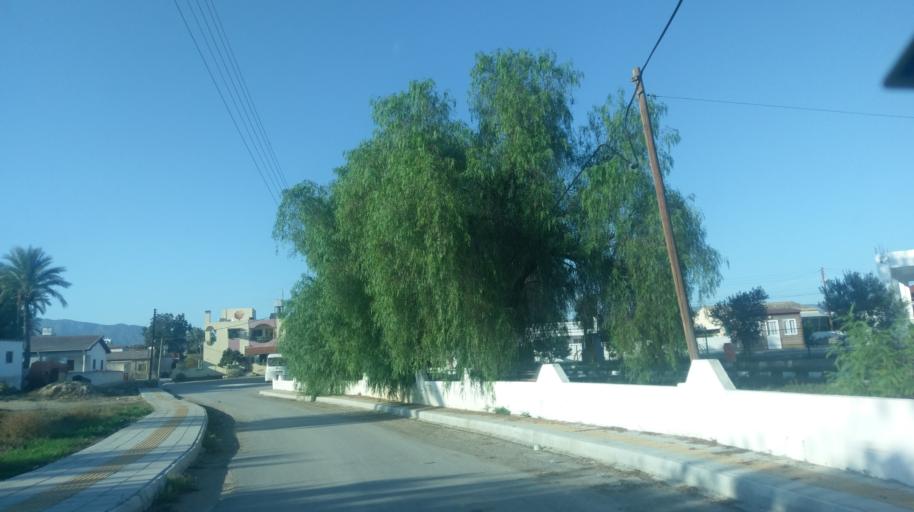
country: CY
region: Ammochostos
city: Lefkonoiko
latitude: 35.2639
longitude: 33.6624
